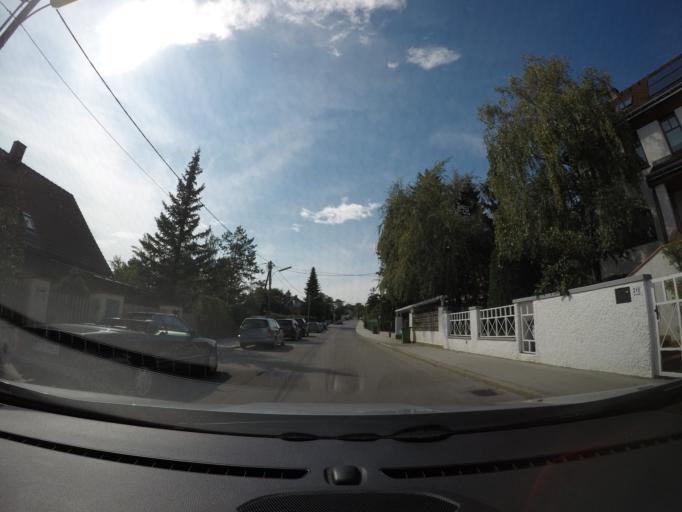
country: AT
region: Lower Austria
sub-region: Politischer Bezirk Modling
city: Perchtoldsdorf
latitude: 48.2038
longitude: 16.2706
